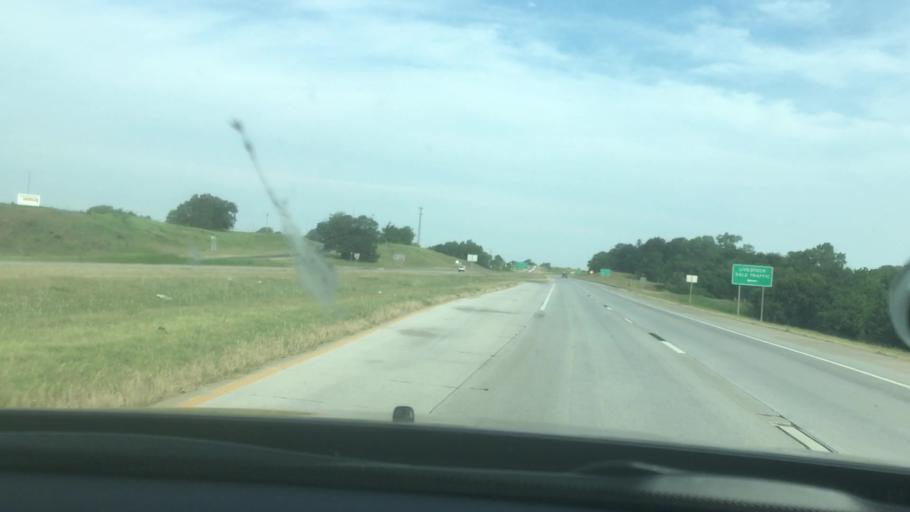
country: US
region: Oklahoma
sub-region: Pontotoc County
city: Ada
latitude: 34.7812
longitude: -96.7145
